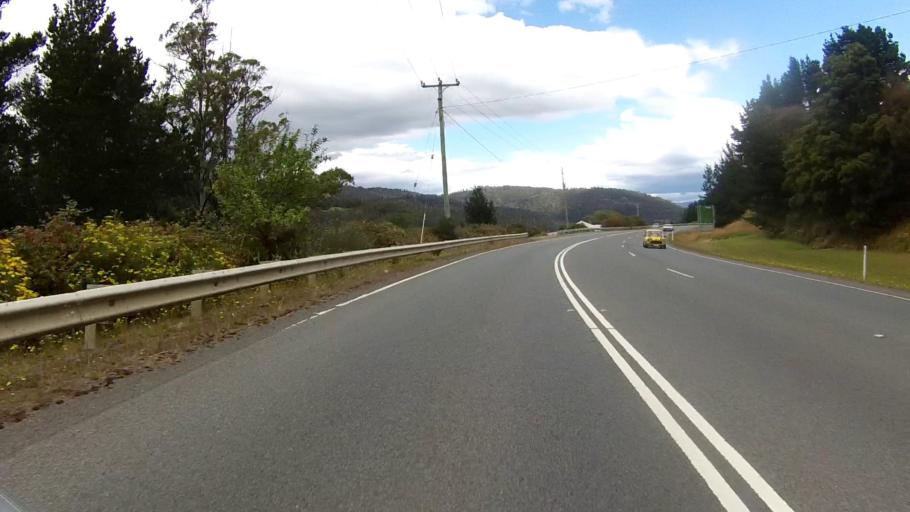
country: AU
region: Tasmania
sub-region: Huon Valley
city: Huonville
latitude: -42.9762
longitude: 147.1444
